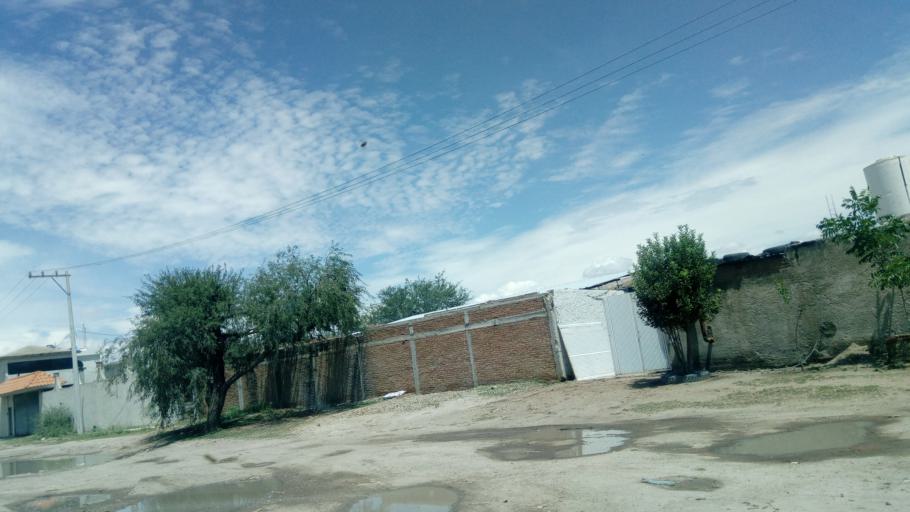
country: MX
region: Durango
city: Victoria de Durango
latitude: 24.0138
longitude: -104.5898
